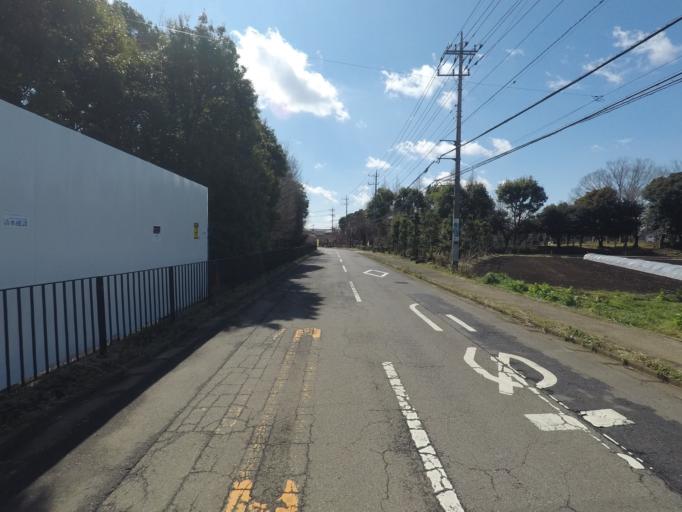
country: JP
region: Ibaraki
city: Naka
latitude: 36.0514
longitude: 140.1138
